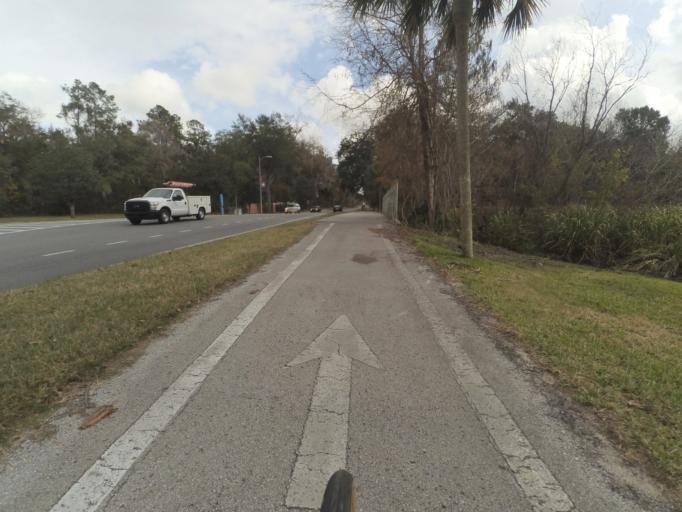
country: US
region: Florida
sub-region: Alachua County
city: Gainesville
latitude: 29.6448
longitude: -82.3603
